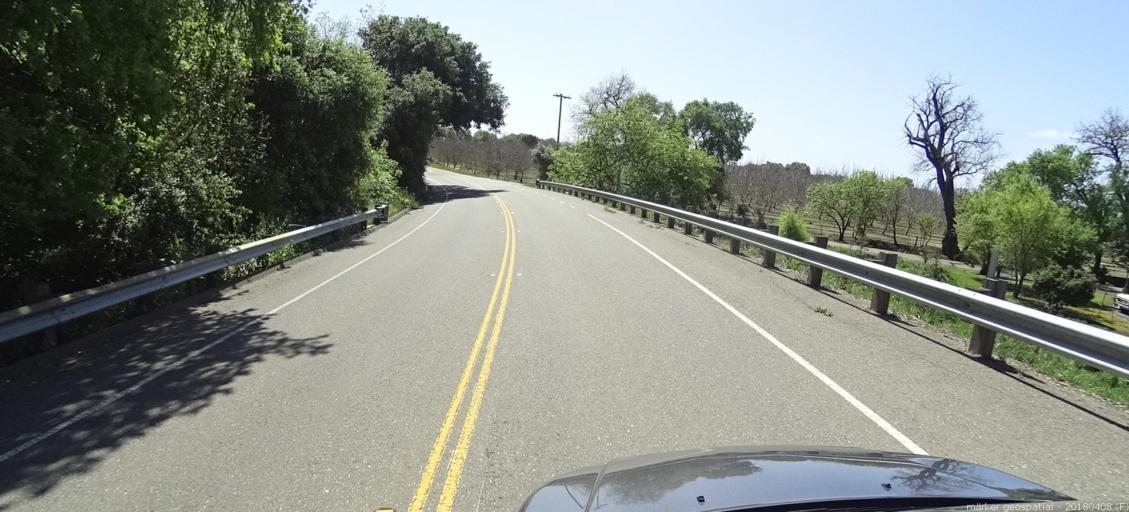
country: US
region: California
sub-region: San Joaquin County
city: Thornton
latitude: 38.2538
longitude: -121.4400
